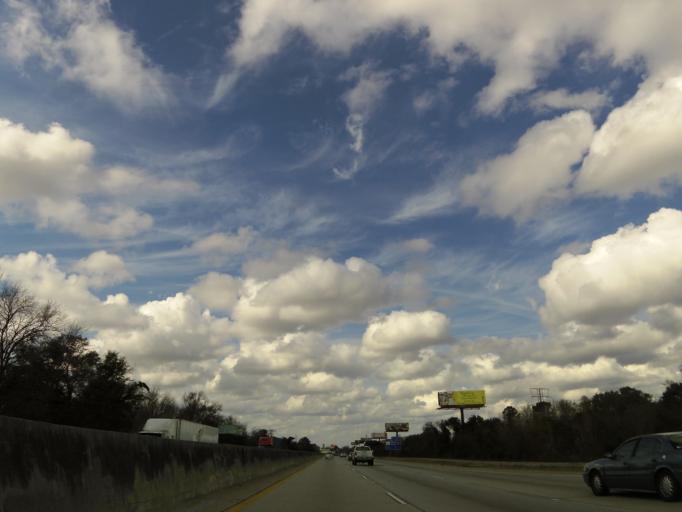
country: US
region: South Carolina
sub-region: Charleston County
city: North Charleston
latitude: 32.8560
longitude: -79.9894
